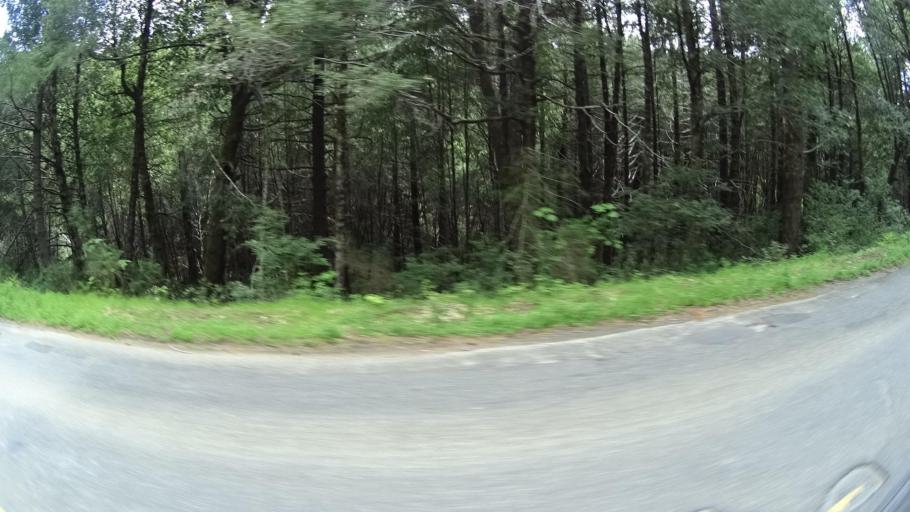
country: US
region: California
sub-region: Humboldt County
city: Redway
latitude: 40.0733
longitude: -123.9575
